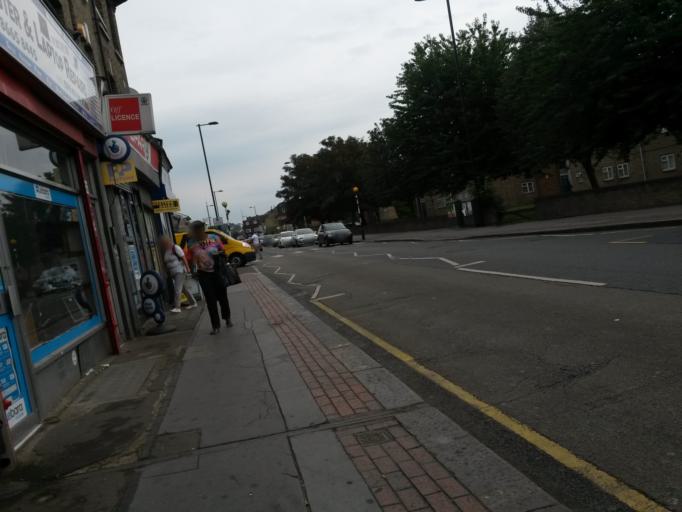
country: GB
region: England
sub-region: Greater London
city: Croydon
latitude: 51.3852
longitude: -0.0975
